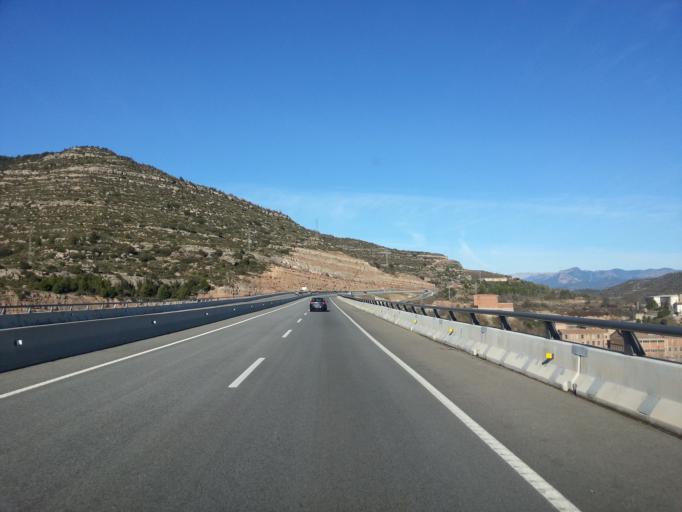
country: ES
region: Catalonia
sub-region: Provincia de Barcelona
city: Puig-reig
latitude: 41.9835
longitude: 1.8850
